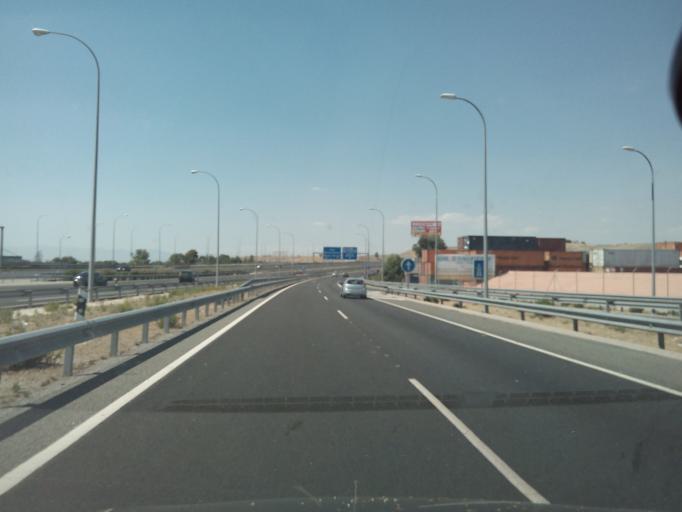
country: ES
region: Madrid
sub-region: Provincia de Madrid
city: San Fernando de Henares
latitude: 40.4533
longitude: -3.5190
